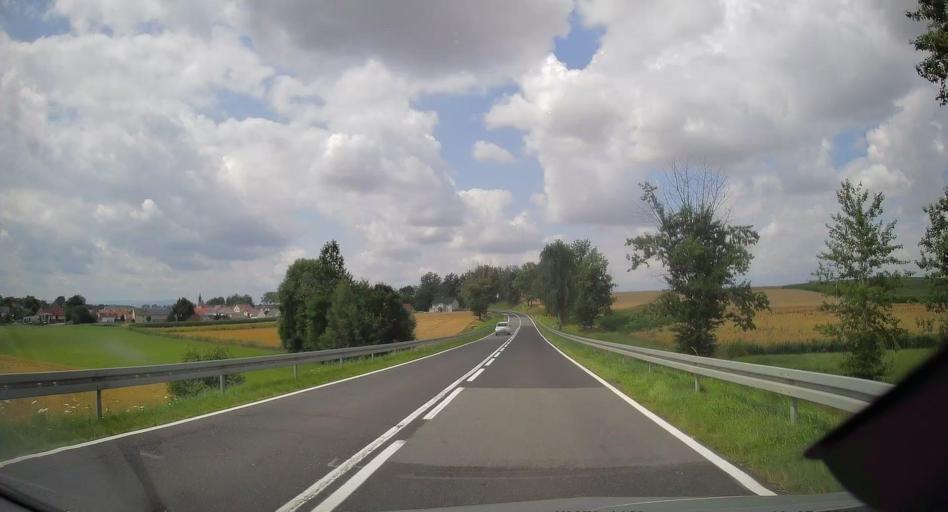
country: PL
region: Opole Voivodeship
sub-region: Powiat prudnicki
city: Raclawice Slaskie
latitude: 50.3460
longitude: 17.7477
